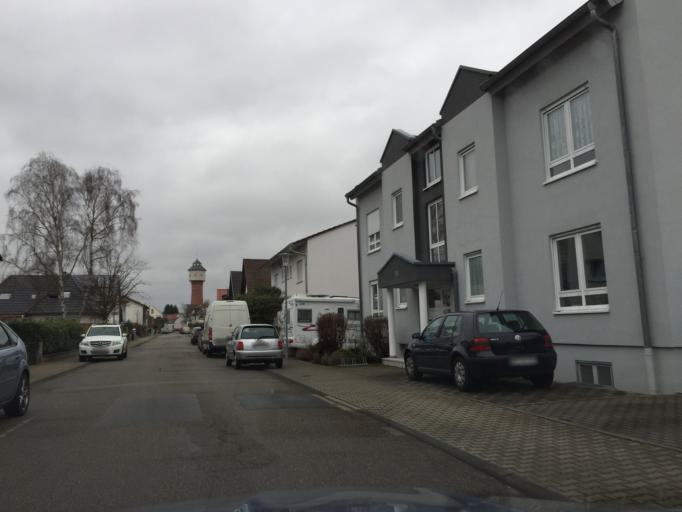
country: DE
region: Baden-Wuerttemberg
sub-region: Karlsruhe Region
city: Plankstadt
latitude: 49.3872
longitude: 8.5935
